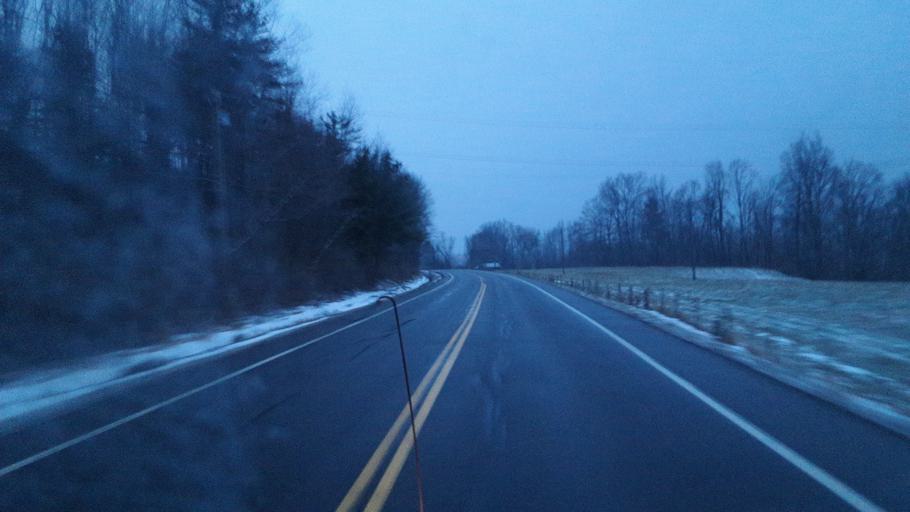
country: US
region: New York
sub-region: Allegany County
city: Belmont
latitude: 42.3139
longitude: -78.0966
